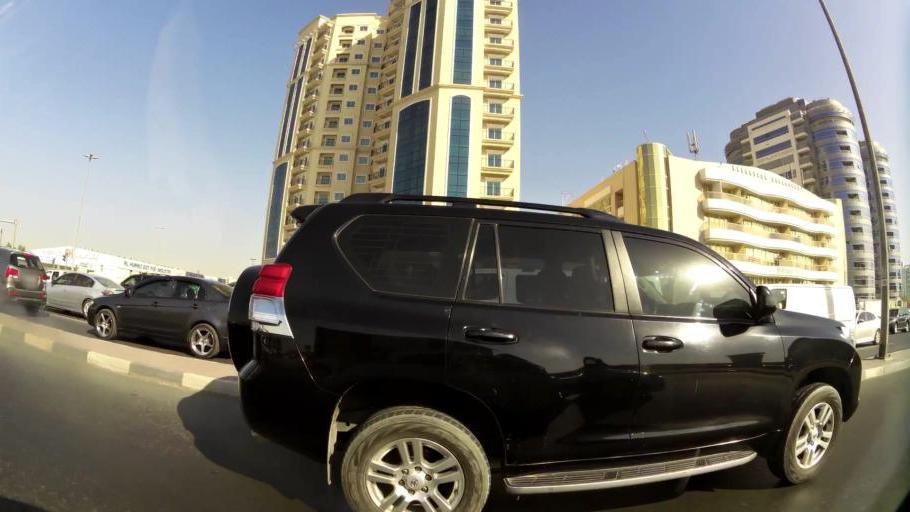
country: AE
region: Ash Shariqah
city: Sharjah
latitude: 25.2926
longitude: 55.3952
